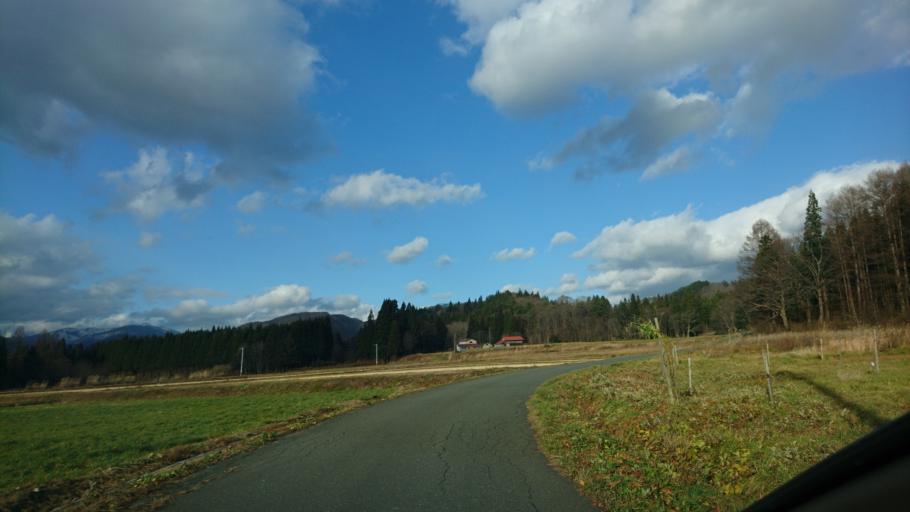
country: JP
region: Akita
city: Kakunodatemachi
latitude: 39.4614
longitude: 140.7867
